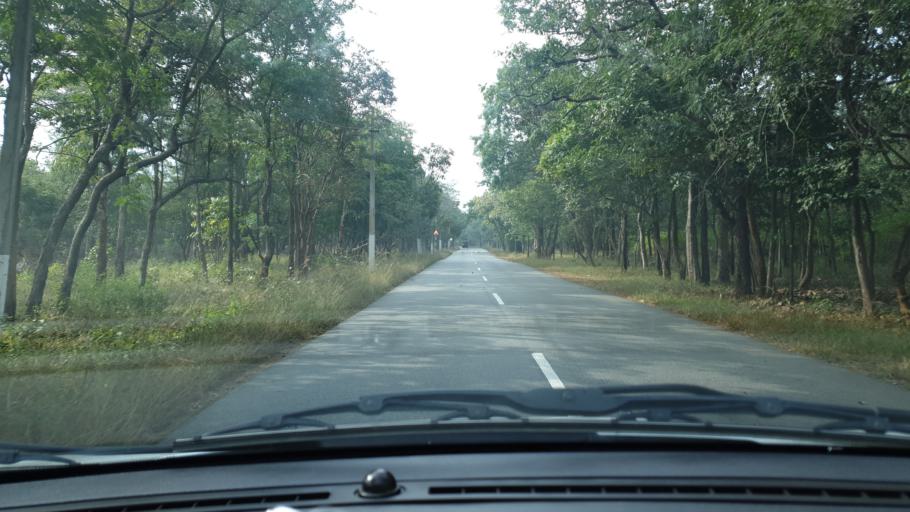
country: IN
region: Andhra Pradesh
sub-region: Kurnool
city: Srisailam
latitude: 16.2853
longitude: 78.7277
